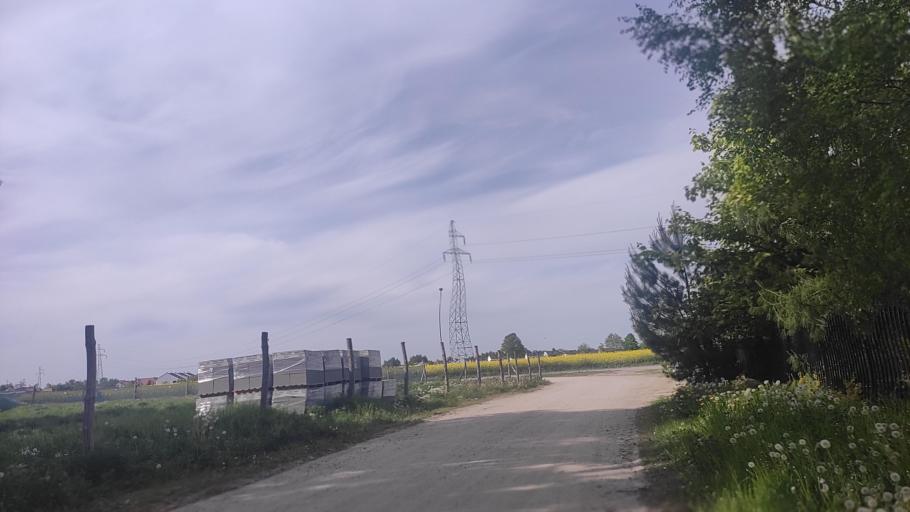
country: PL
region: Greater Poland Voivodeship
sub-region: Powiat poznanski
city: Swarzedz
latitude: 52.4129
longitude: 17.0986
